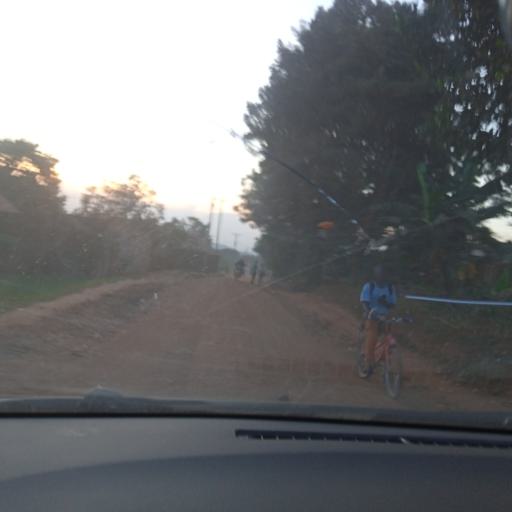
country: UG
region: Central Region
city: Masaka
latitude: -0.3111
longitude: 31.7653
